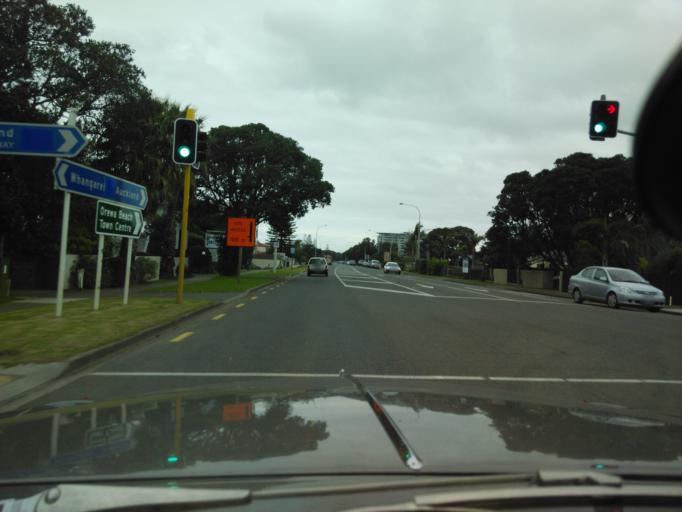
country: NZ
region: Auckland
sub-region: Auckland
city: Rothesay Bay
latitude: -36.5806
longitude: 174.6929
